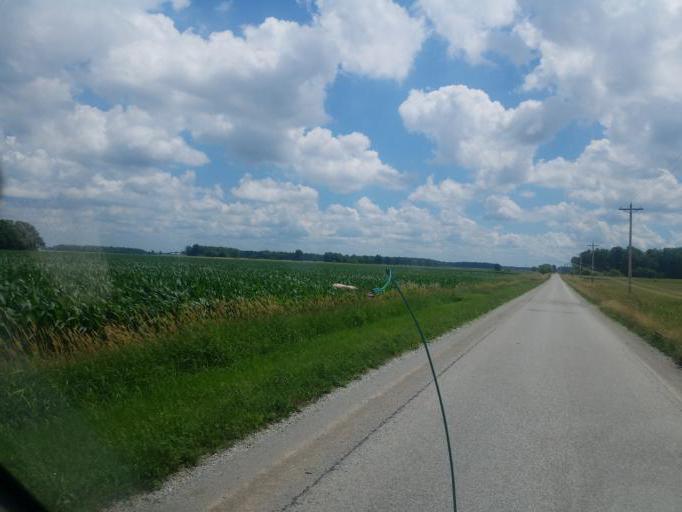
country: US
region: Ohio
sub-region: Huron County
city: Willard
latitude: 41.0381
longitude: -82.8310
